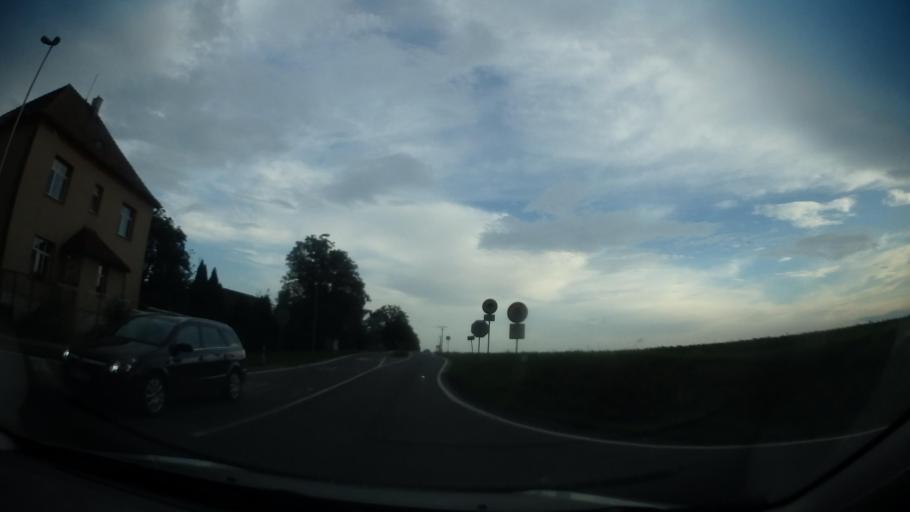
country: CZ
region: Olomoucky
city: Dub nad Moravou
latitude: 49.4810
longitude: 17.2725
